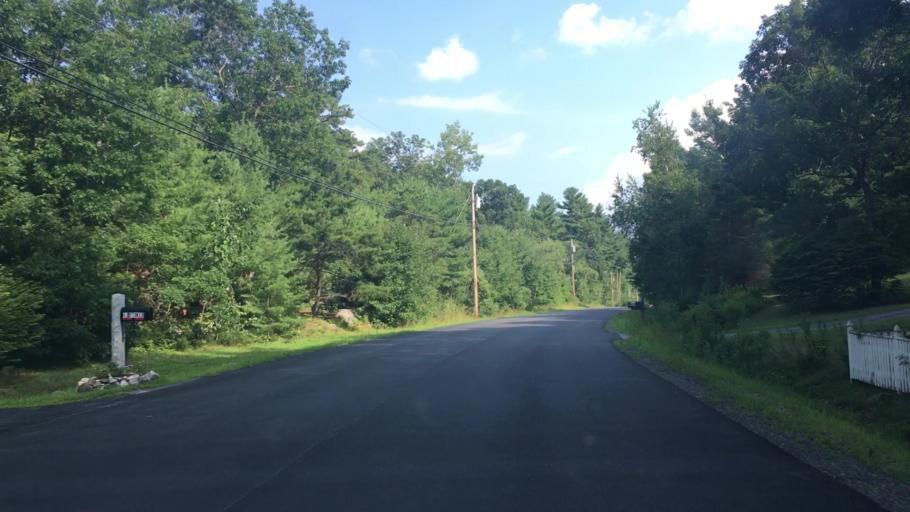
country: US
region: New Hampshire
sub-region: Rockingham County
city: Derry Village
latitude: 42.9373
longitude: -71.3262
